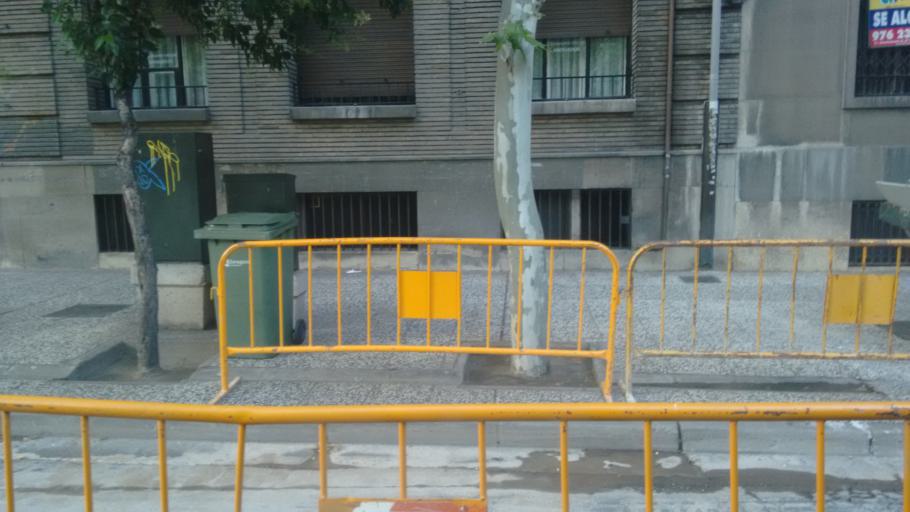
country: ES
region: Aragon
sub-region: Provincia de Zaragoza
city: Zaragoza
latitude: 41.6471
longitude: -0.8800
